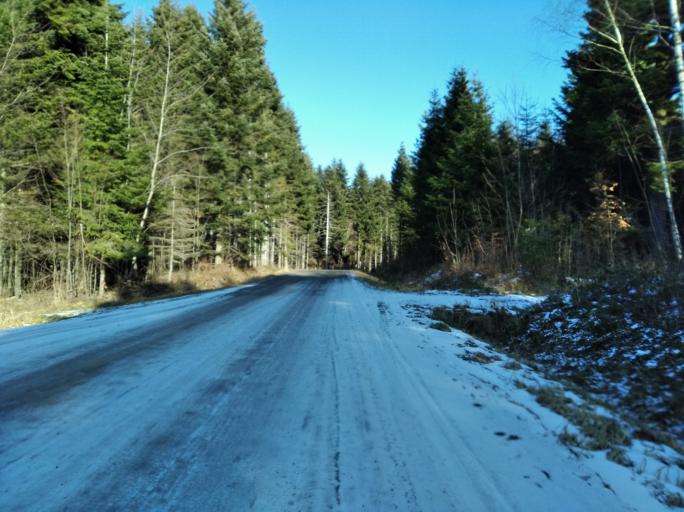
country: PL
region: Subcarpathian Voivodeship
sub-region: Powiat rzeszowski
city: Straszydle
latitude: 49.8727
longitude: 21.9769
